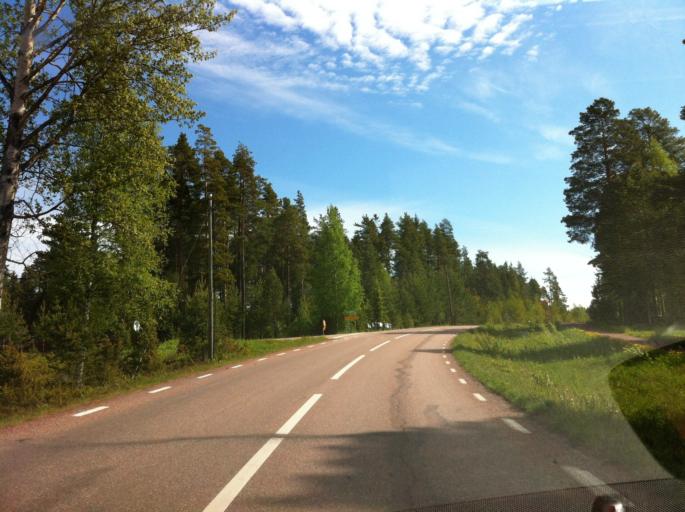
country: SE
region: Dalarna
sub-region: Mora Kommun
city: Mora
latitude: 60.9006
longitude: 14.5778
